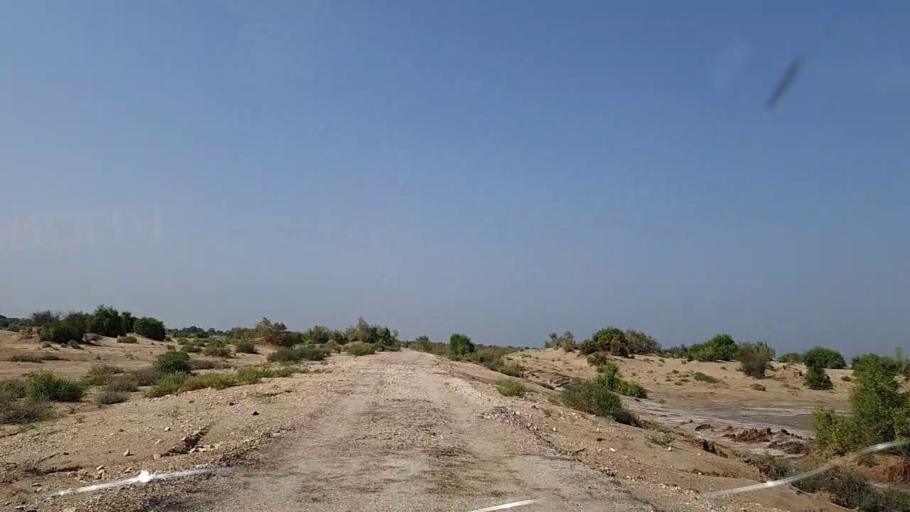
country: PK
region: Sindh
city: Khanpur
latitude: 27.6973
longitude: 69.3848
